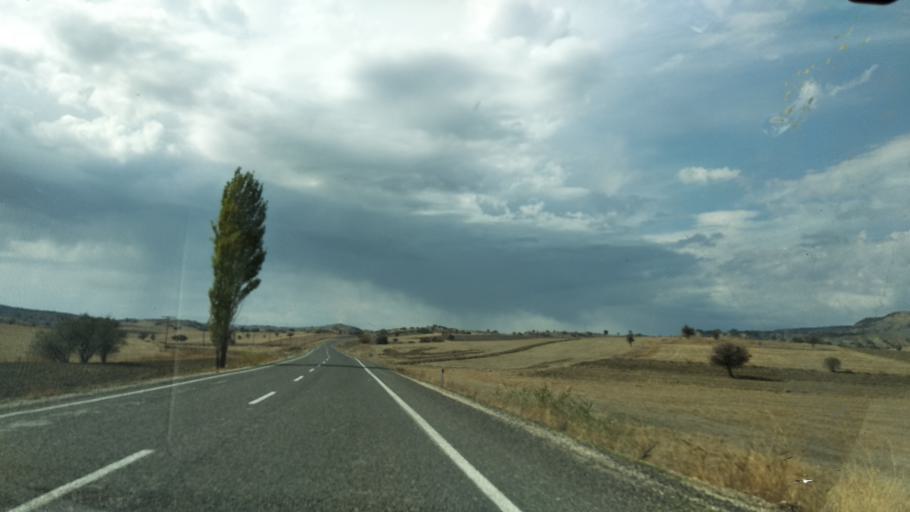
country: TR
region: Bolu
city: Seben
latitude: 40.3924
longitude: 31.5481
